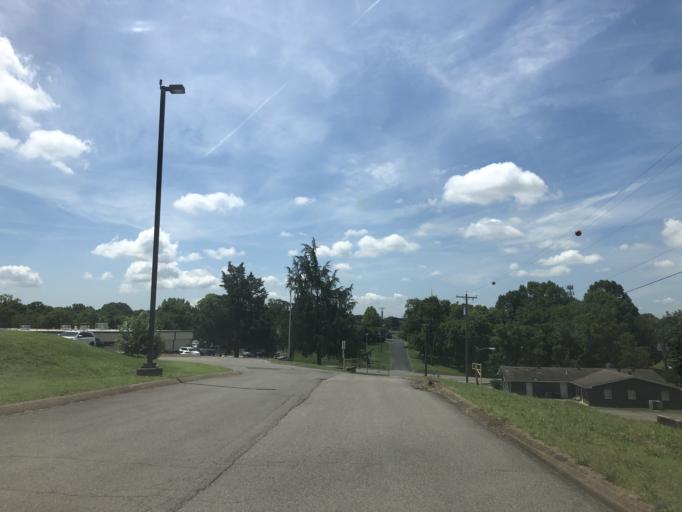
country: US
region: Tennessee
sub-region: Davidson County
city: Lakewood
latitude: 36.2553
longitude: -86.6843
